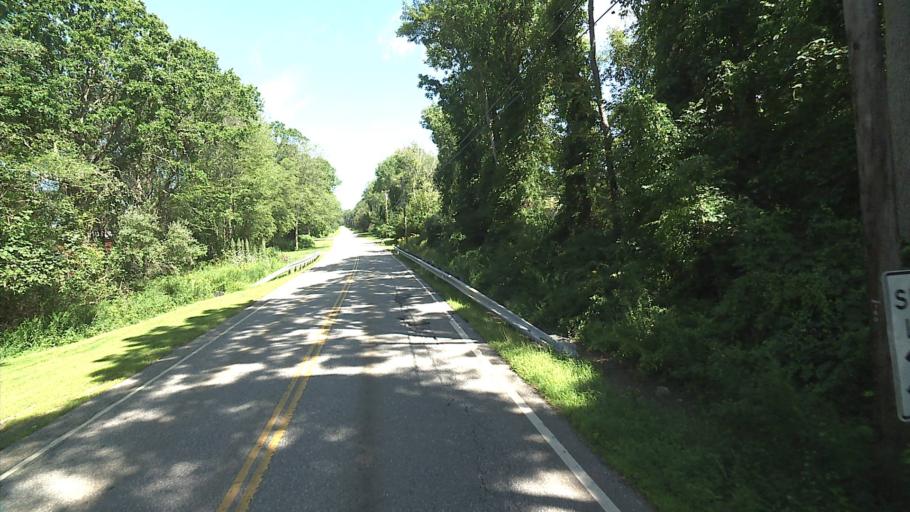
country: US
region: Connecticut
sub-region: Windham County
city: Windham
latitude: 41.7096
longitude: -72.0675
